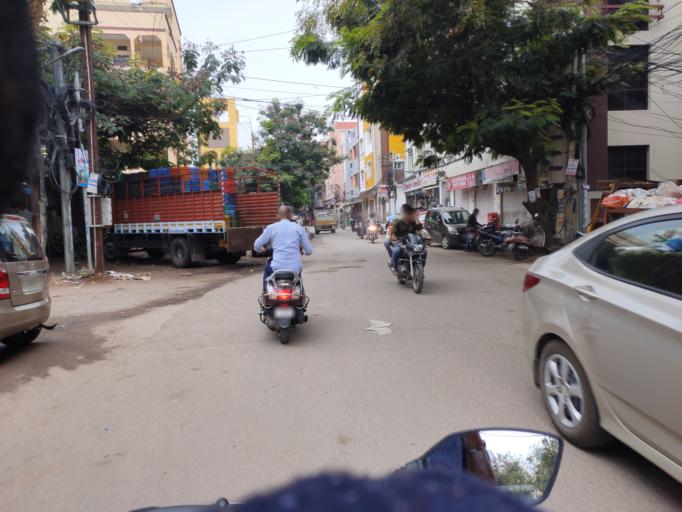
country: IN
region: Telangana
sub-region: Rangareddi
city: Kukatpalli
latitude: 17.4499
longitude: 78.4451
